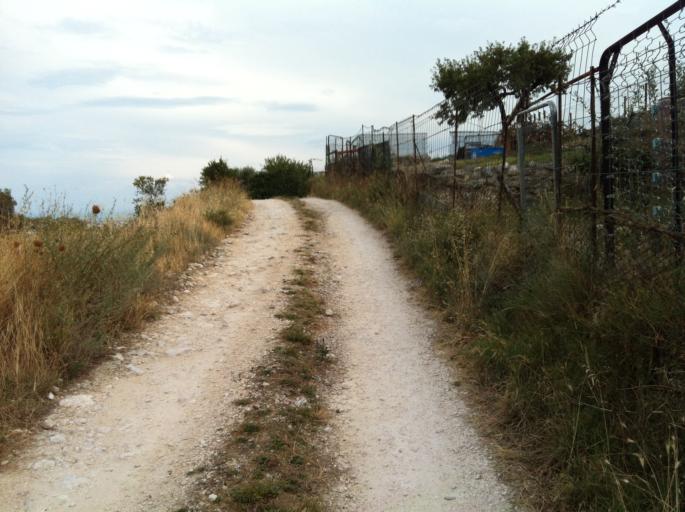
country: IT
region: Apulia
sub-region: Provincia di Foggia
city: Manfredonia
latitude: 41.6599
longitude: 15.9127
